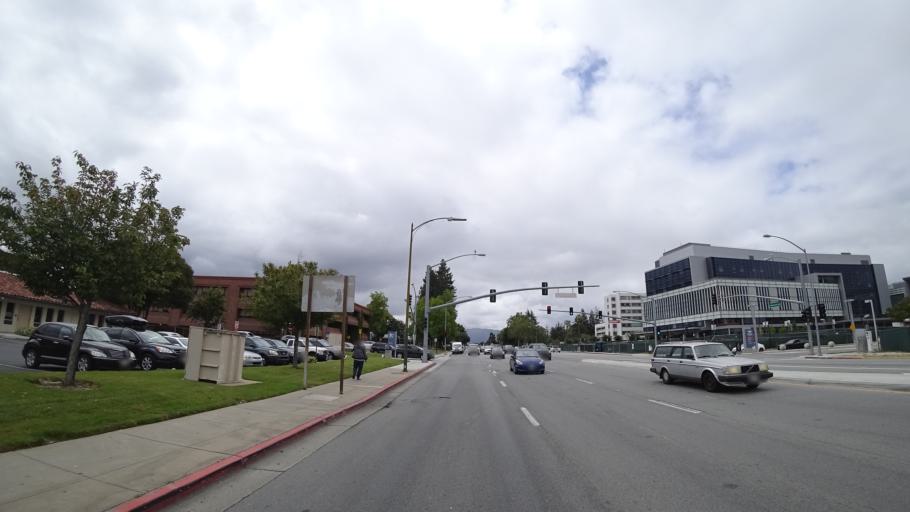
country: US
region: California
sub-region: Santa Clara County
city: Burbank
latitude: 37.3149
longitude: -121.9317
